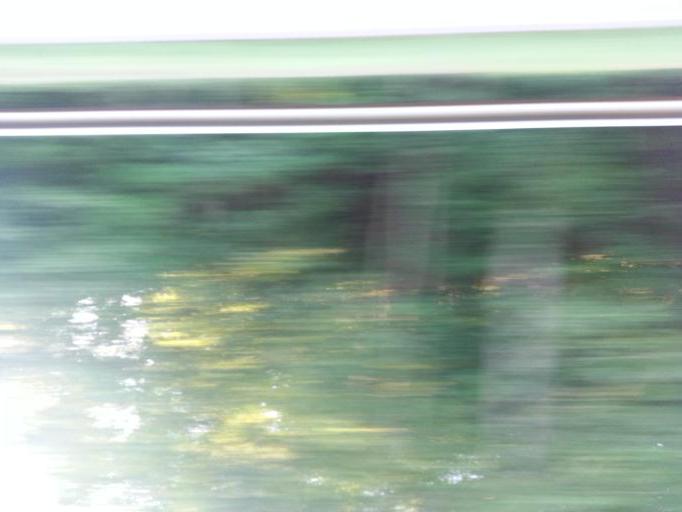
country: US
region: Tennessee
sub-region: Loudon County
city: Greenback
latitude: 35.6582
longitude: -84.2234
